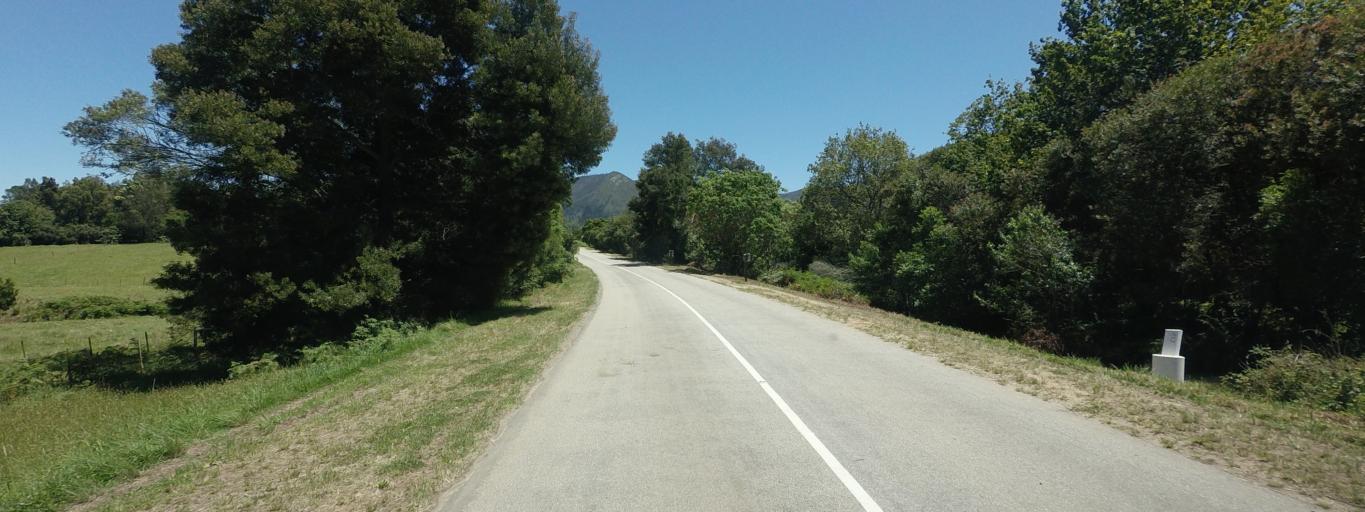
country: ZA
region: Western Cape
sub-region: Eden District Municipality
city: Plettenberg Bay
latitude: -33.9378
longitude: 23.5081
